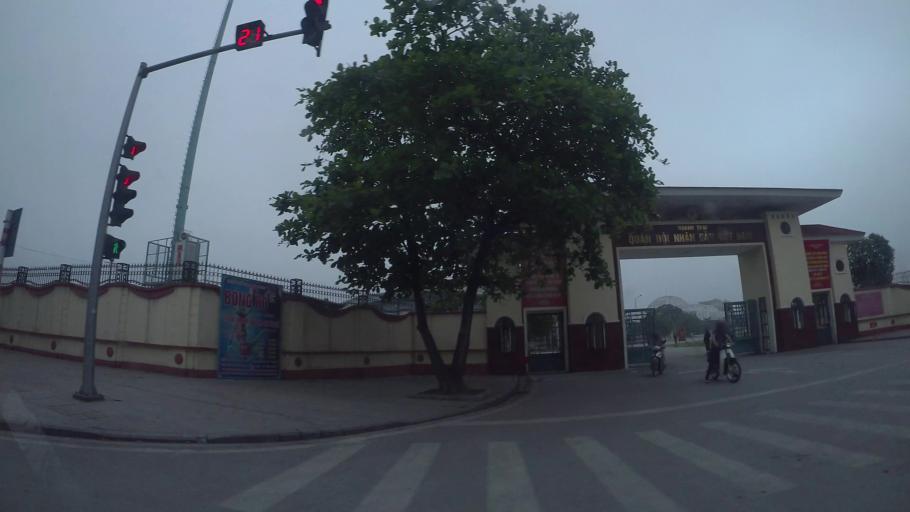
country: VN
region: Ha Noi
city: Dong Da
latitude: 20.9971
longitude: 105.8295
